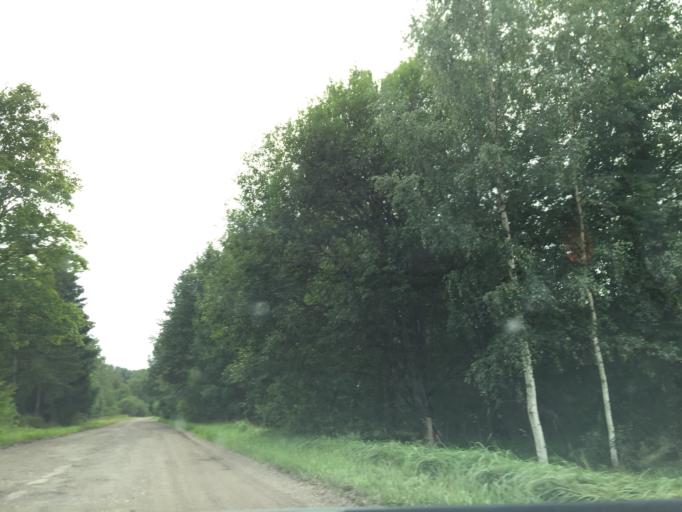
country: LV
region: Lielvarde
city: Lielvarde
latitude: 56.7553
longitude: 24.8410
